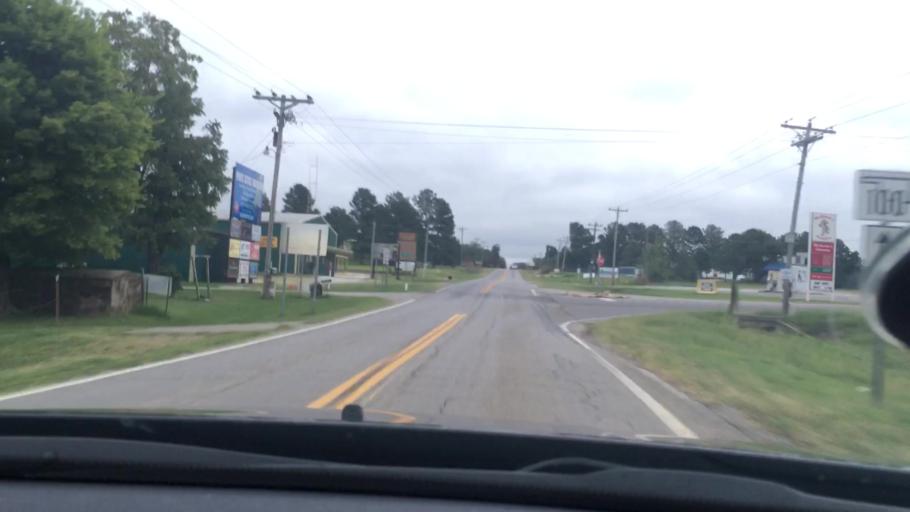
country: US
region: Oklahoma
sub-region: Sequoyah County
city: Vian
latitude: 35.6097
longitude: -94.9770
